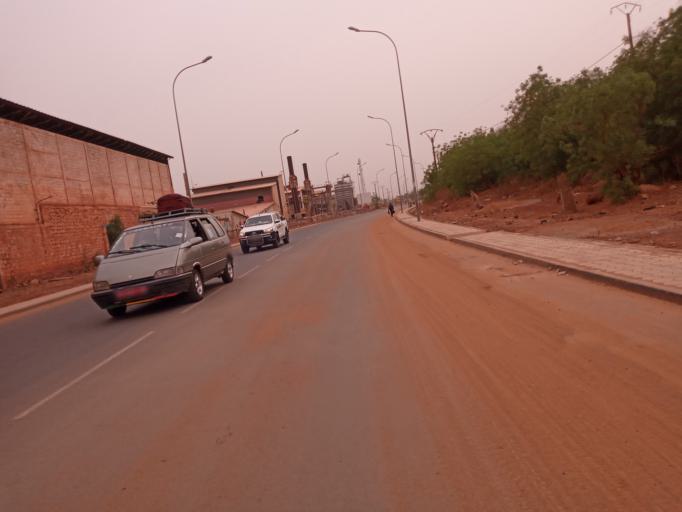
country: ML
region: Koulikoro
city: Koulikoro
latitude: 12.8548
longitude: -7.5635
